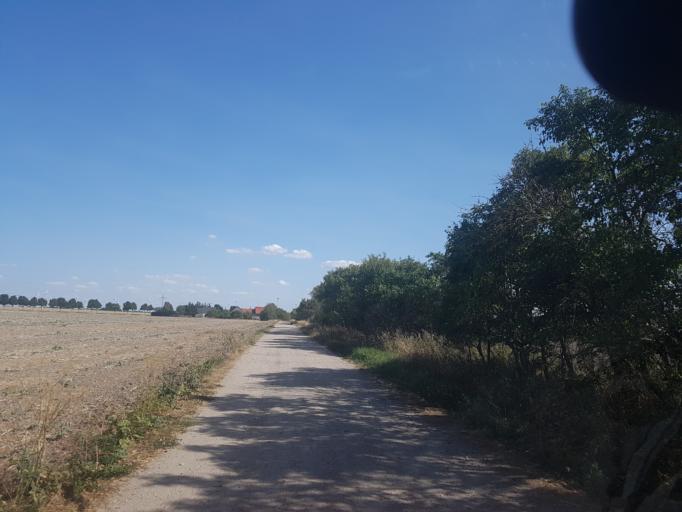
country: DE
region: Saxony-Anhalt
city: Kropstadt
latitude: 52.0182
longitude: 12.7854
